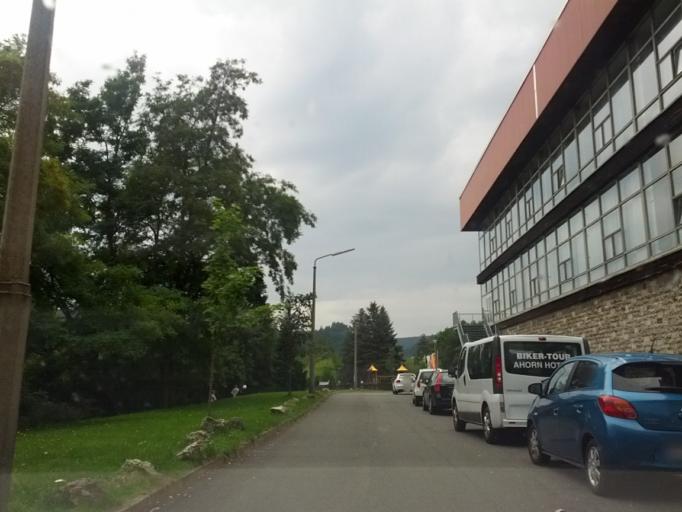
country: DE
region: Thuringia
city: Friedrichroda
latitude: 50.8648
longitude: 10.5685
